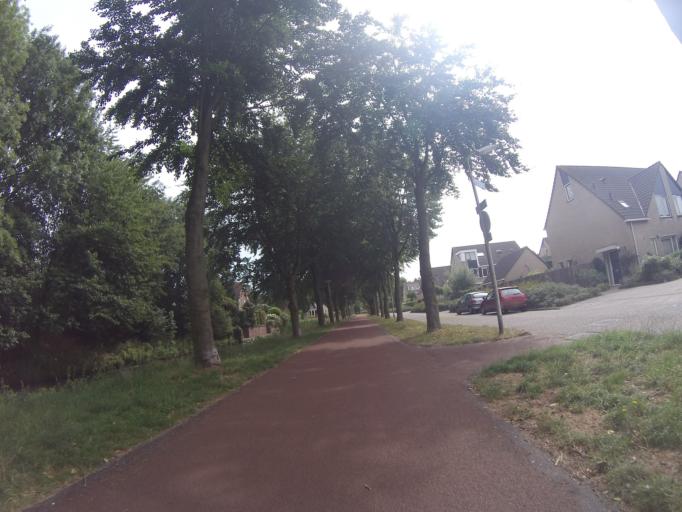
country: NL
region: Utrecht
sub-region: Gemeente Amersfoort
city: Hoogland
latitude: 52.1825
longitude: 5.3799
